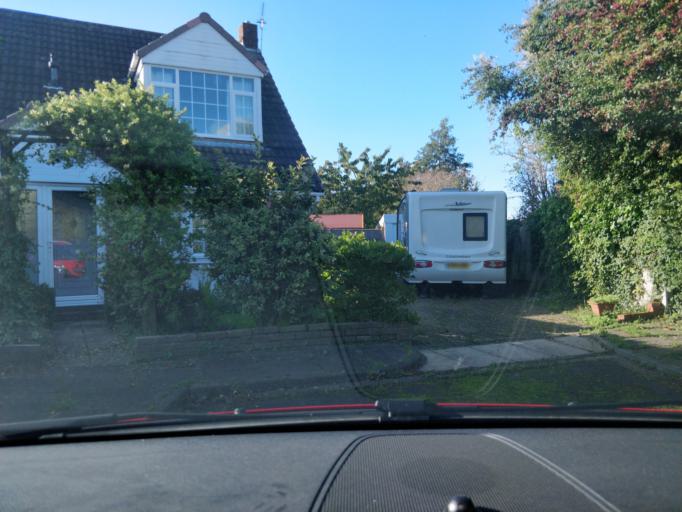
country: GB
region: England
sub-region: Lancashire
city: Banks
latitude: 53.6796
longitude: -2.9507
